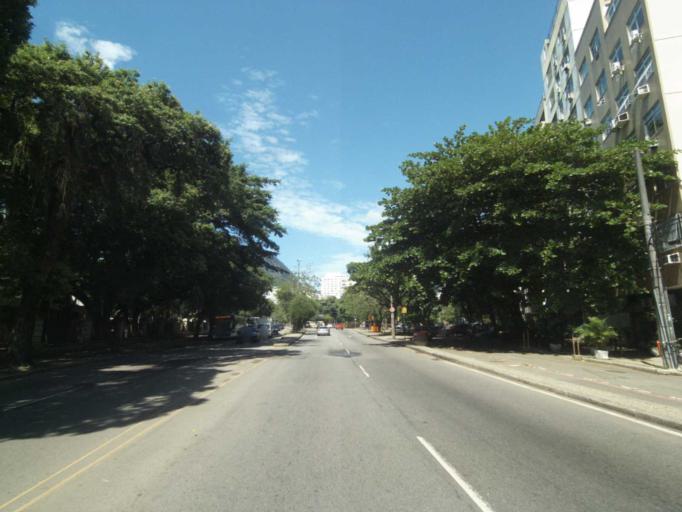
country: BR
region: Rio de Janeiro
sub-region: Rio De Janeiro
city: Rio de Janeiro
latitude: -22.9725
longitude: -43.2246
